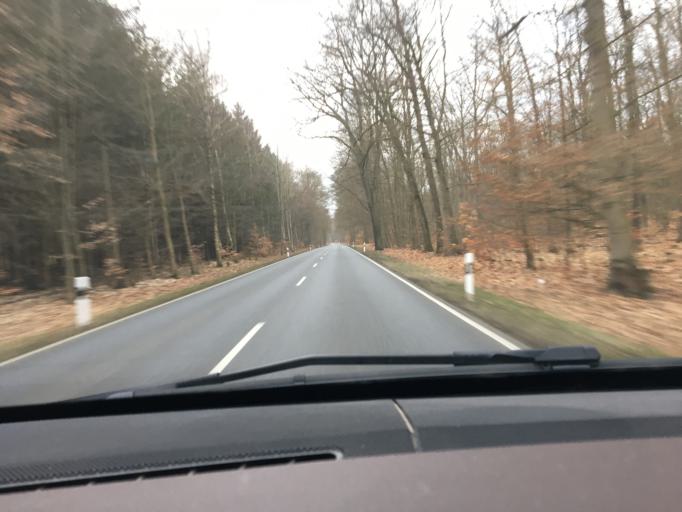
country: DE
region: Brandenburg
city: Marienwerder
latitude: 52.8683
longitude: 13.5032
